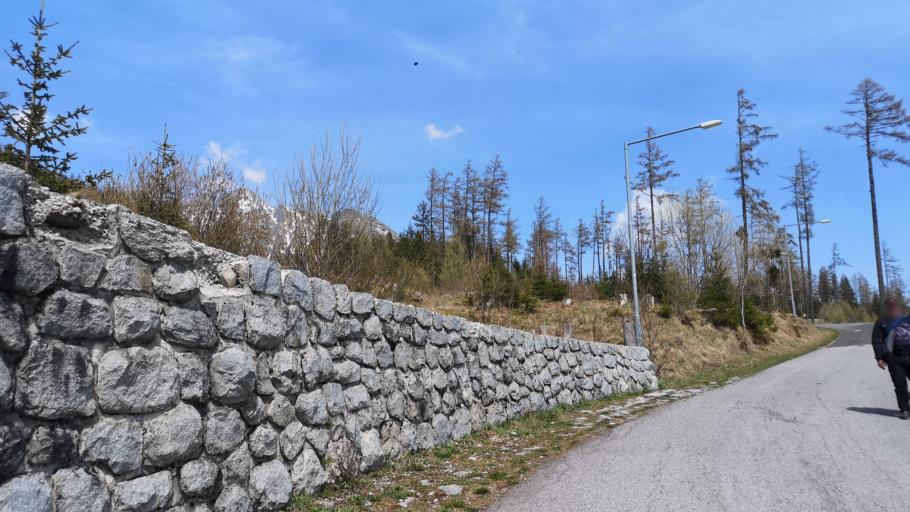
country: SK
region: Presovsky
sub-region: Okres Poprad
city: Vysoke Tatry
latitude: 49.1548
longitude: 20.2239
